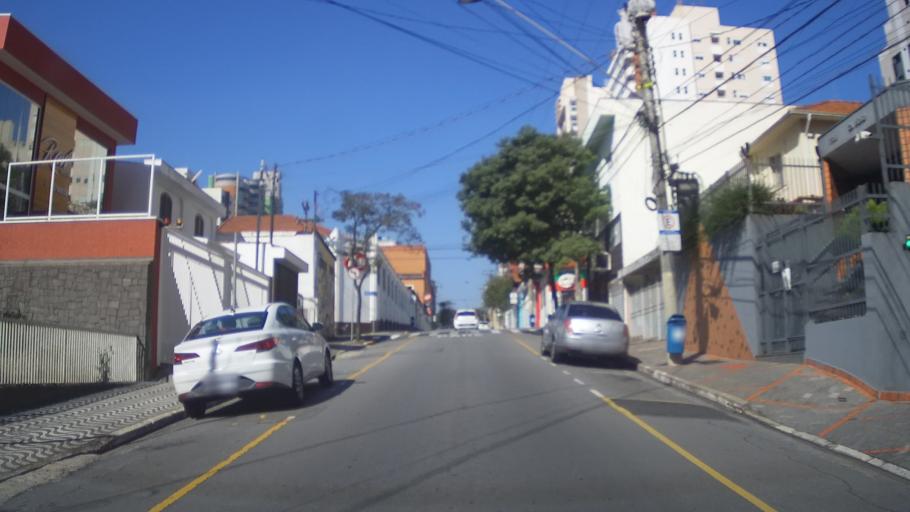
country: BR
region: Sao Paulo
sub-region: Sao Caetano Do Sul
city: Sao Caetano do Sul
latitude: -23.6211
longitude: -46.5662
